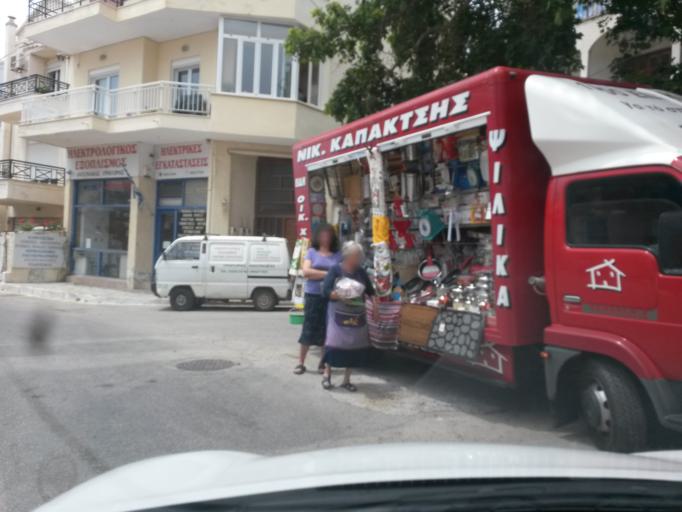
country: GR
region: North Aegean
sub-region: Nomos Lesvou
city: Plomarion
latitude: 38.9730
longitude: 26.3799
